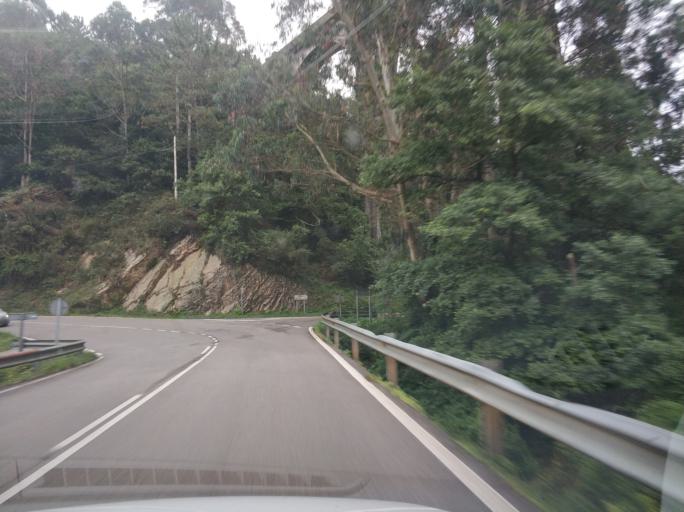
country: ES
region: Asturias
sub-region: Province of Asturias
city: Cudillero
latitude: 43.5527
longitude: -6.1919
